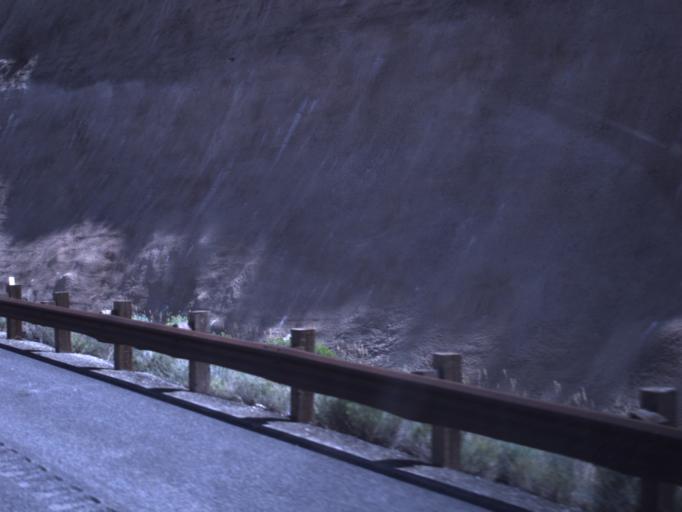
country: US
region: Utah
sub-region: Wasatch County
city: Midway
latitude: 40.4054
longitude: -111.5244
